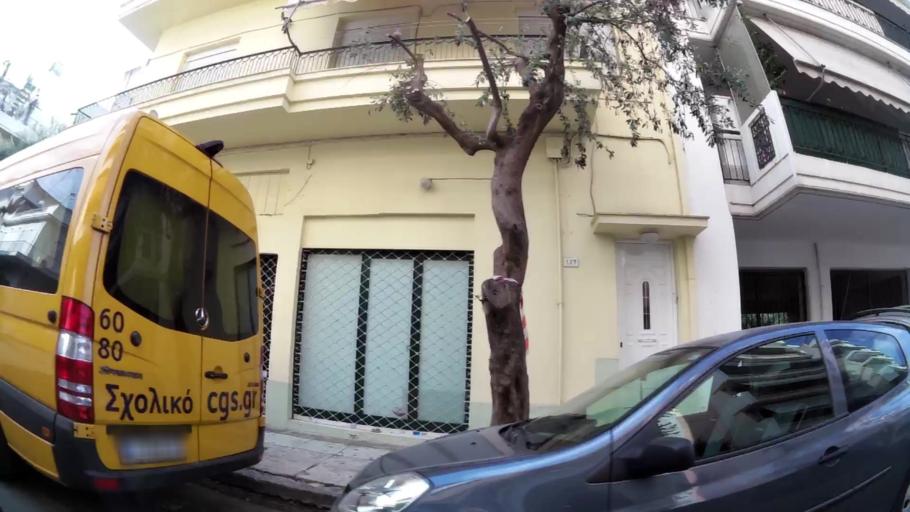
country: GR
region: Attica
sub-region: Nomarchia Athinas
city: Kallithea
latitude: 37.9606
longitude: 23.7020
